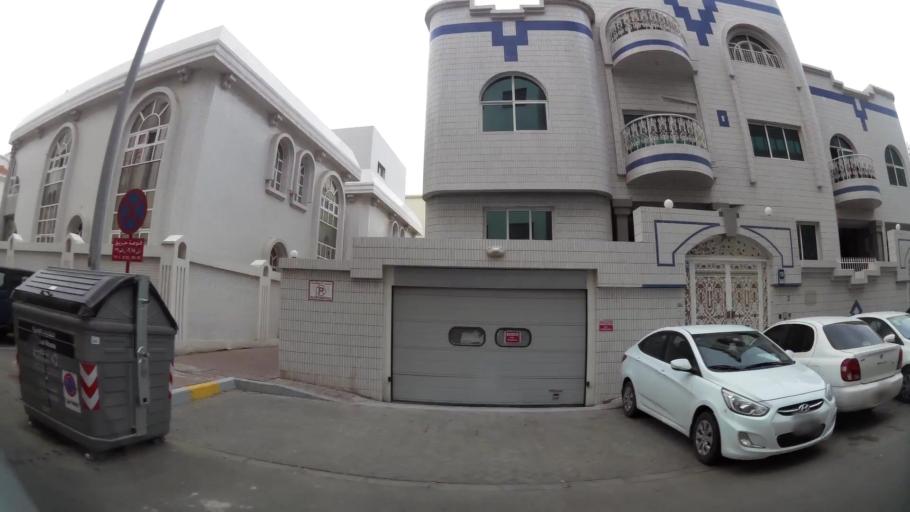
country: AE
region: Abu Dhabi
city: Abu Dhabi
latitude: 24.4815
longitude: 54.3766
